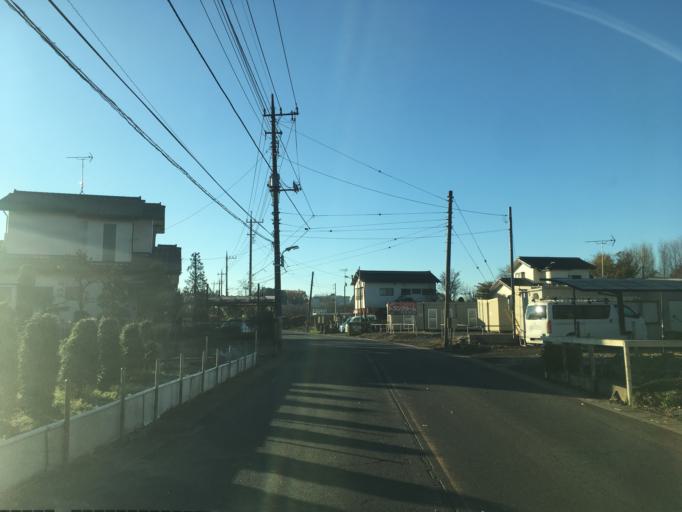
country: JP
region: Saitama
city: Tokorozawa
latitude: 35.7966
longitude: 139.4157
